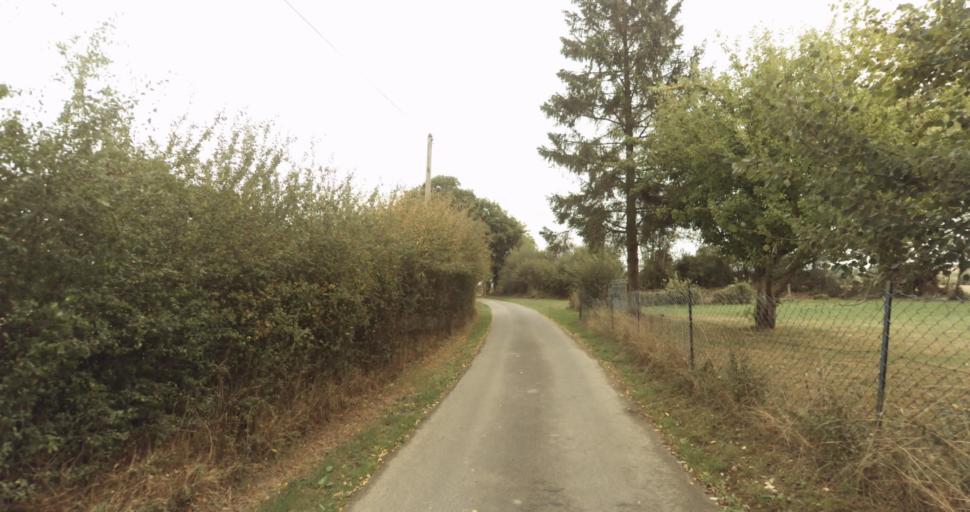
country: FR
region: Lower Normandy
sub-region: Departement de l'Orne
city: Gace
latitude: 48.8140
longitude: 0.3556
